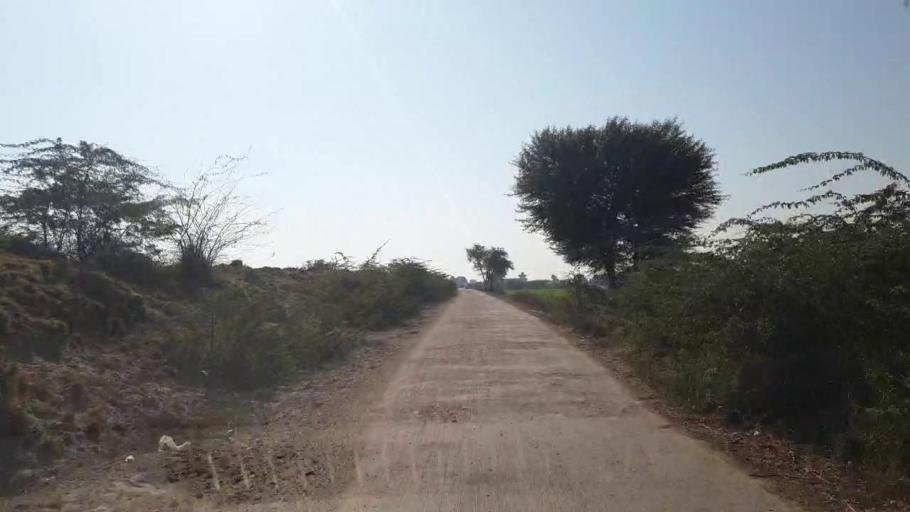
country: PK
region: Sindh
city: Shahpur Chakar
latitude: 26.0829
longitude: 68.6475
